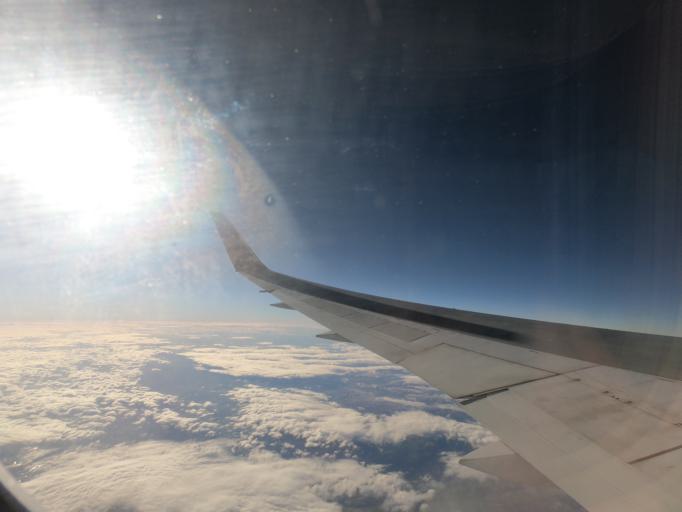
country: GB
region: England
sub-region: City and Borough of Wakefield
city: Castleford
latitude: 53.7088
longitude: -1.3649
